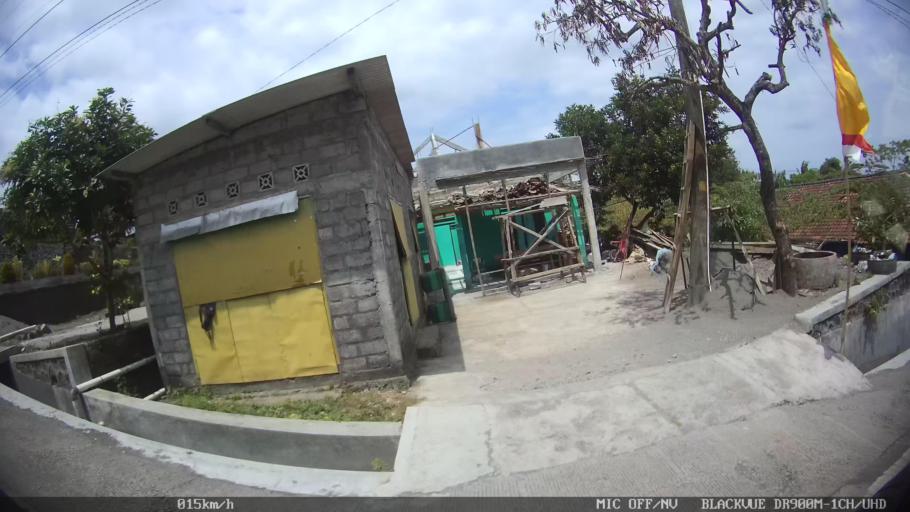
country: ID
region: Central Java
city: Candi Prambanan
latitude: -7.7838
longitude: 110.5065
